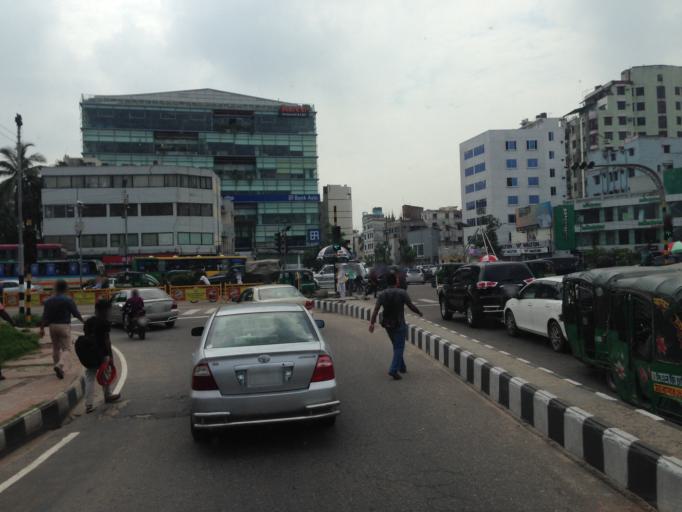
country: BD
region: Dhaka
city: Azimpur
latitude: 23.7646
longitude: 90.3885
